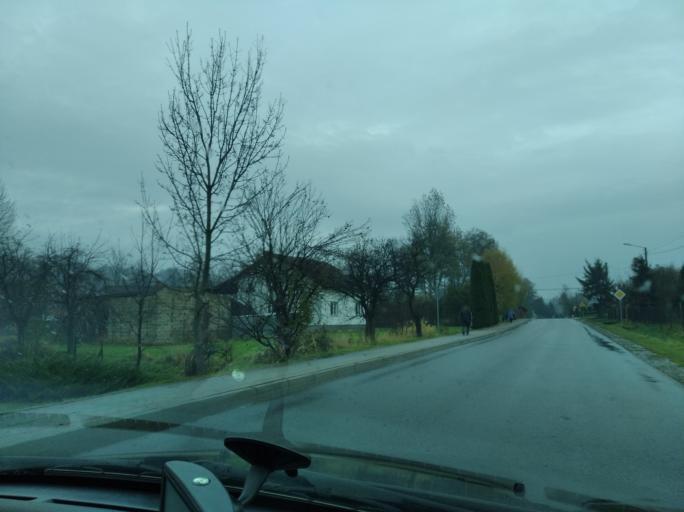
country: PL
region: Subcarpathian Voivodeship
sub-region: Powiat rzeszowski
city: Lubenia
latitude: 49.9248
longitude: 21.9341
